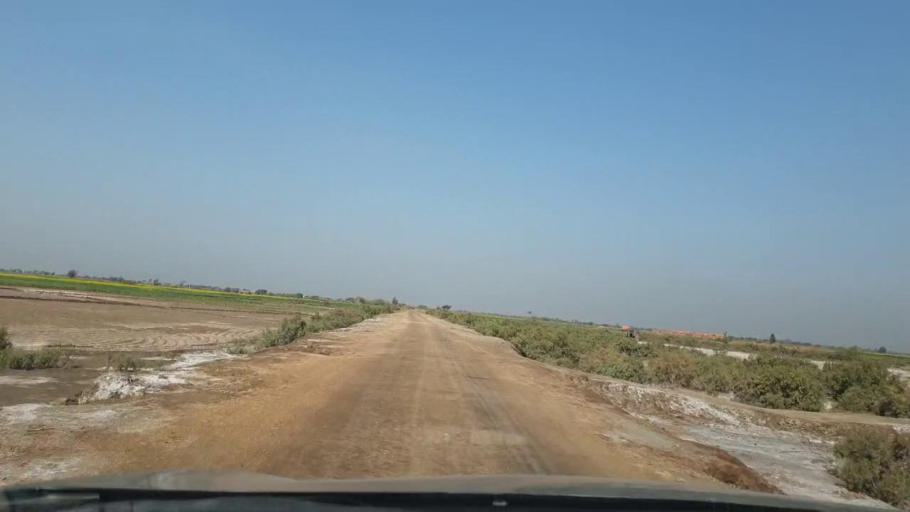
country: PK
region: Sindh
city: Berani
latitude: 25.7049
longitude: 68.8658
